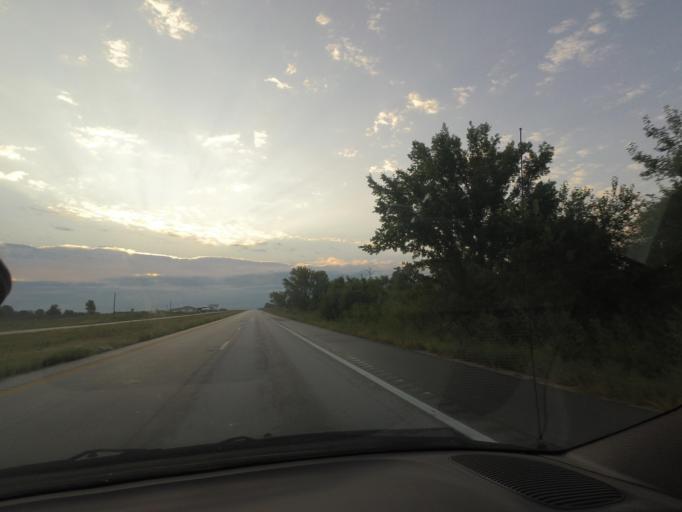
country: US
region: Missouri
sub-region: Shelby County
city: Shelbina
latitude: 39.7381
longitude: -92.2305
